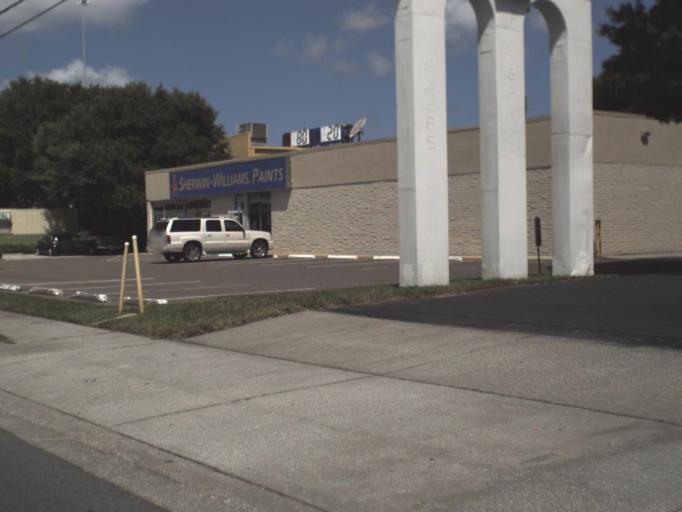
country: US
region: Florida
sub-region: Pinellas County
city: Dunedin
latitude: 28.0195
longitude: -82.7364
